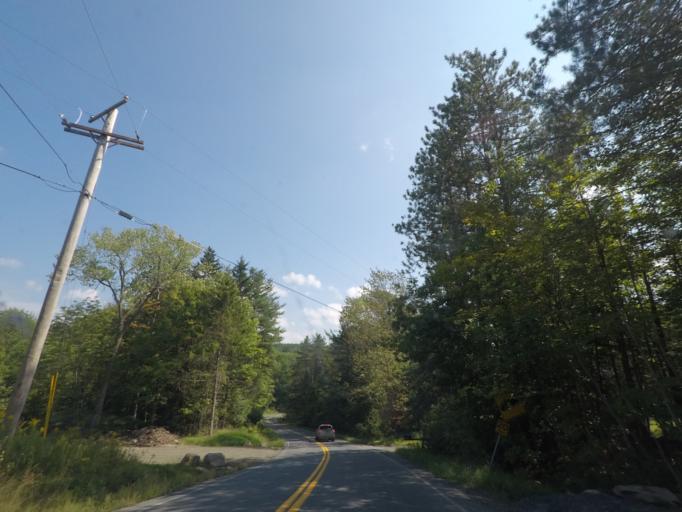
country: US
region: New York
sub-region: Rensselaer County
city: Poestenkill
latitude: 42.7109
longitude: -73.5089
